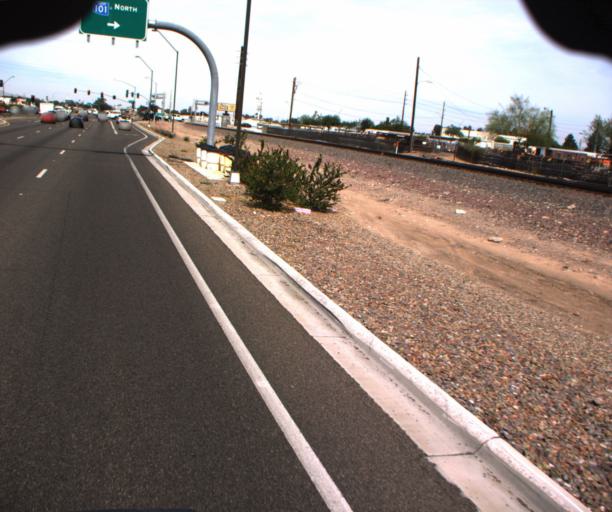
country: US
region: Arizona
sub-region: Maricopa County
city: Sun City
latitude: 33.5922
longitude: -112.2535
